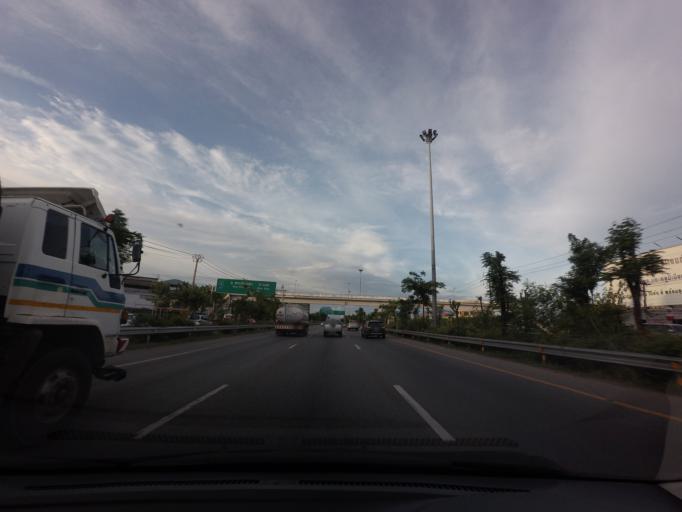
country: TH
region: Bangkok
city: Bang Bon
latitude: 13.6358
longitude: 100.4027
